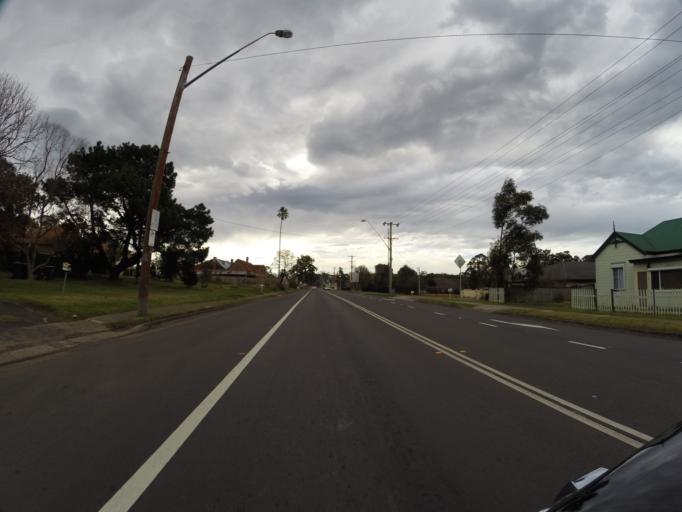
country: AU
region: New South Wales
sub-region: Wollondilly
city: Douglas Park
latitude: -34.2028
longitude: 150.7867
